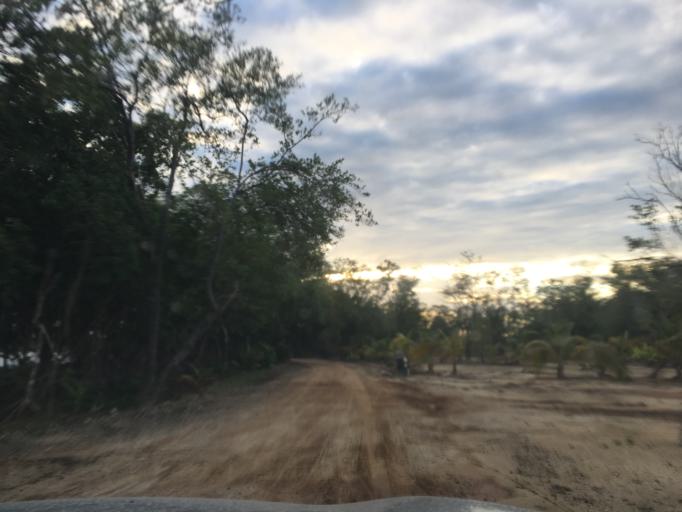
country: BZ
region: Stann Creek
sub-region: Dangriga
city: Dangriga
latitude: 16.8347
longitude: -88.2625
